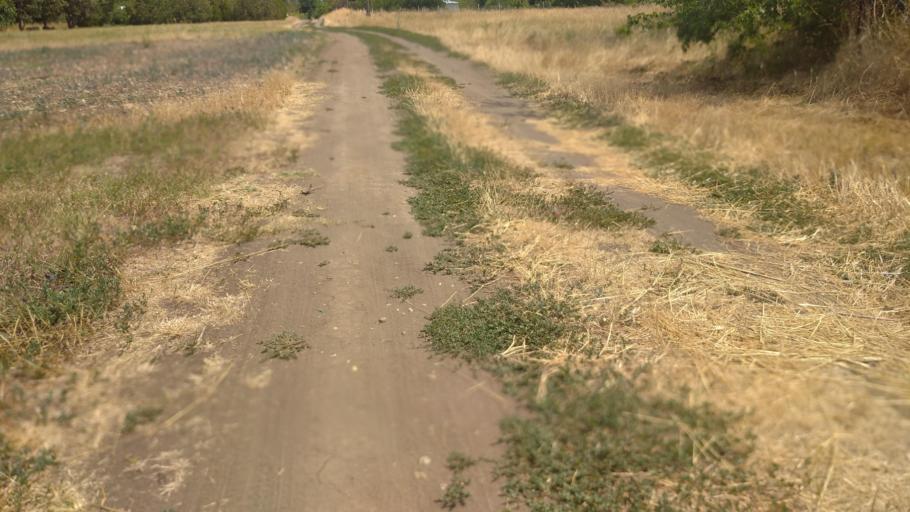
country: HU
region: Bekes
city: Oroshaza
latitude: 46.5606
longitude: 20.6190
